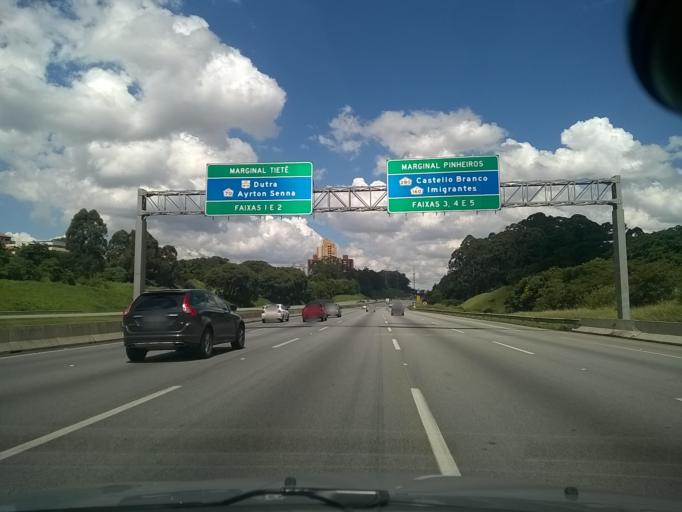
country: BR
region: Sao Paulo
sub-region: Osasco
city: Osasco
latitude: -23.4932
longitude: -46.7332
